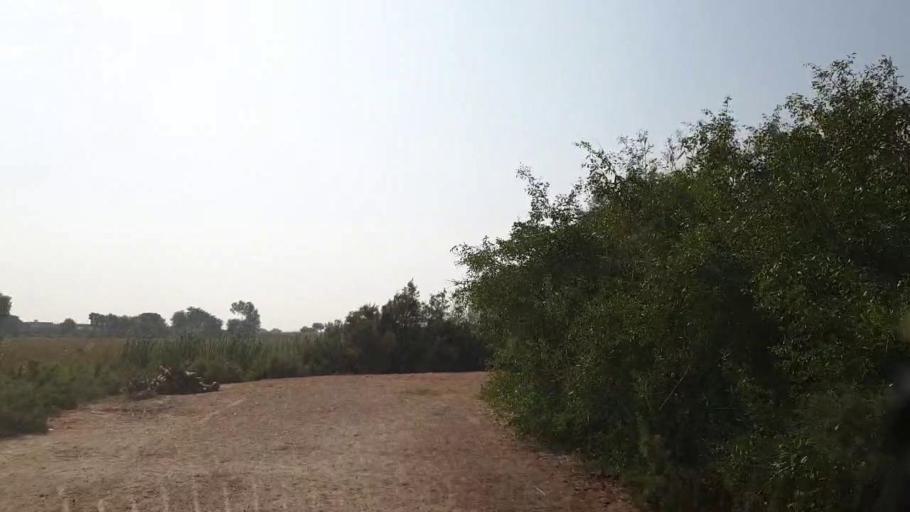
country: PK
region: Sindh
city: Tando Muhammad Khan
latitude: 25.0679
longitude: 68.4290
